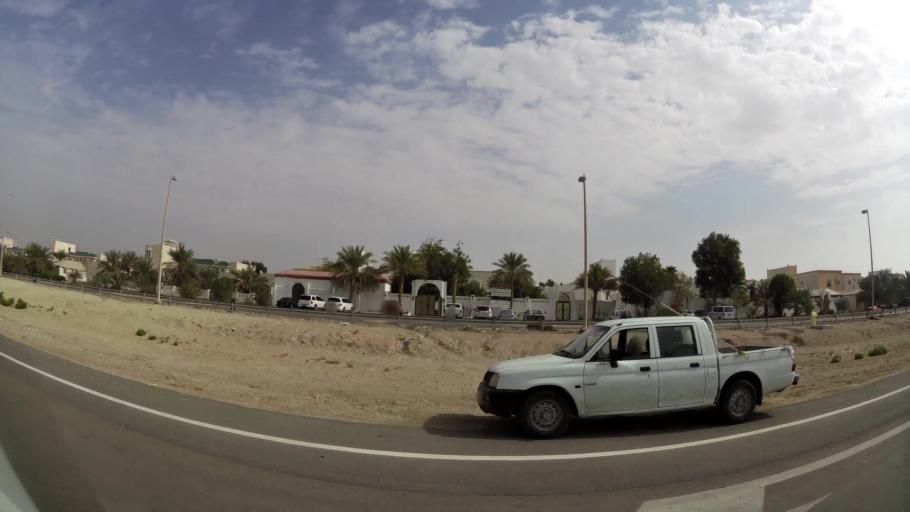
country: AE
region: Abu Dhabi
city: Abu Dhabi
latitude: 24.2817
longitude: 54.6596
